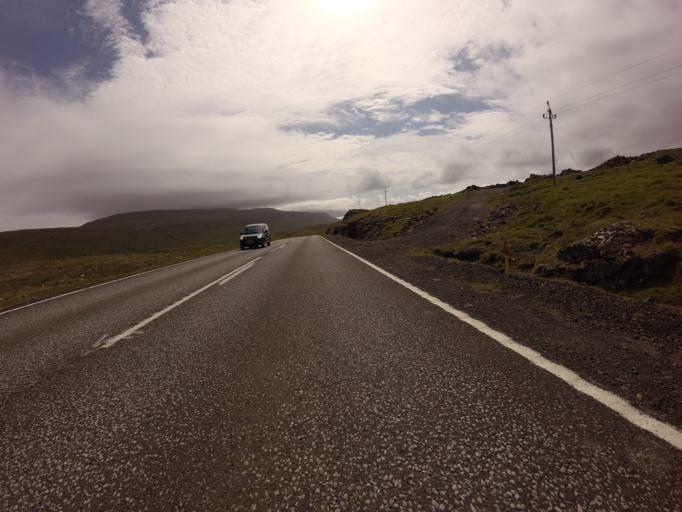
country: FO
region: Sandoy
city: Sandur
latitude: 61.8744
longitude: -6.8573
